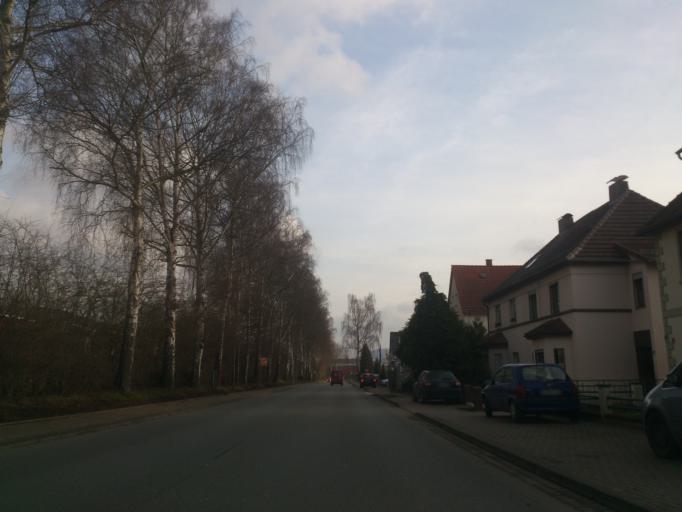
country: DE
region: North Rhine-Westphalia
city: Beverungen
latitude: 51.7111
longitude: 9.2931
